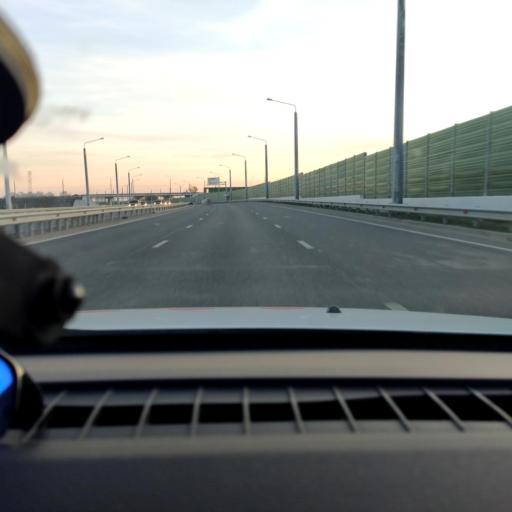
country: RU
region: Samara
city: Samara
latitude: 53.1685
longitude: 50.0854
